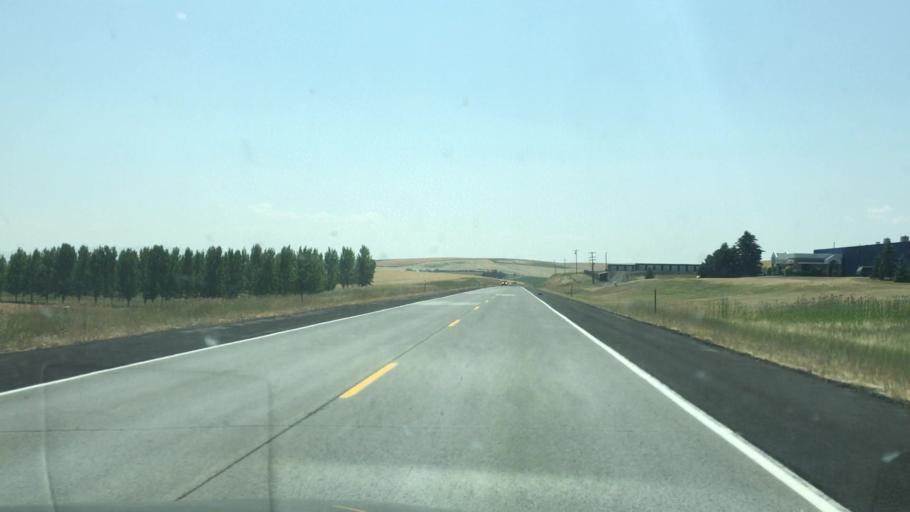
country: US
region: Idaho
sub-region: Lewis County
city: Nezperce
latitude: 46.0794
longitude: -116.3439
